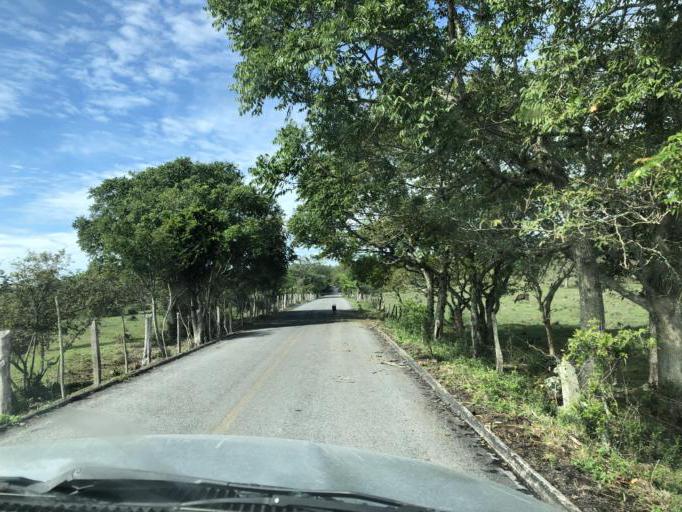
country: MX
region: Veracruz
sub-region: Alto Lucero de Gutierrez Barrios
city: Palma Sola
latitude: 19.8020
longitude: -96.5438
